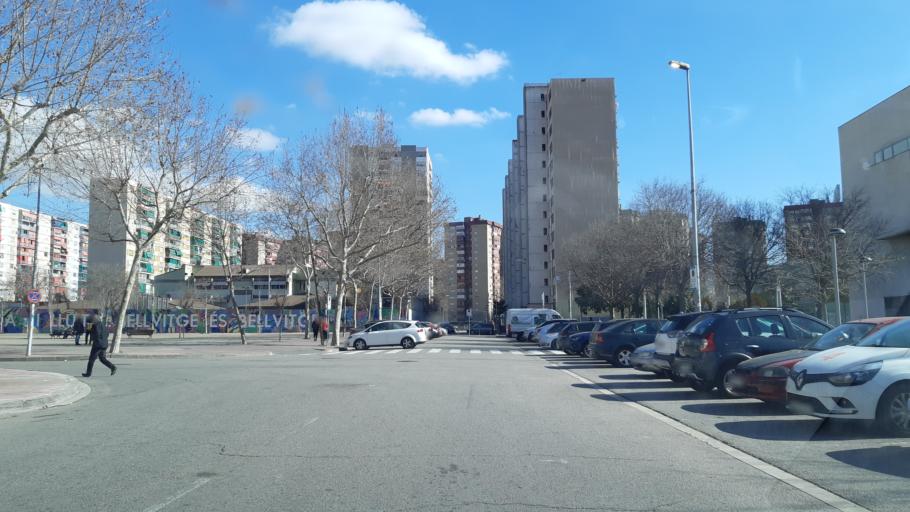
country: ES
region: Catalonia
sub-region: Provincia de Barcelona
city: L'Hospitalet de Llobregat
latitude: 41.3515
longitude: 2.1123
